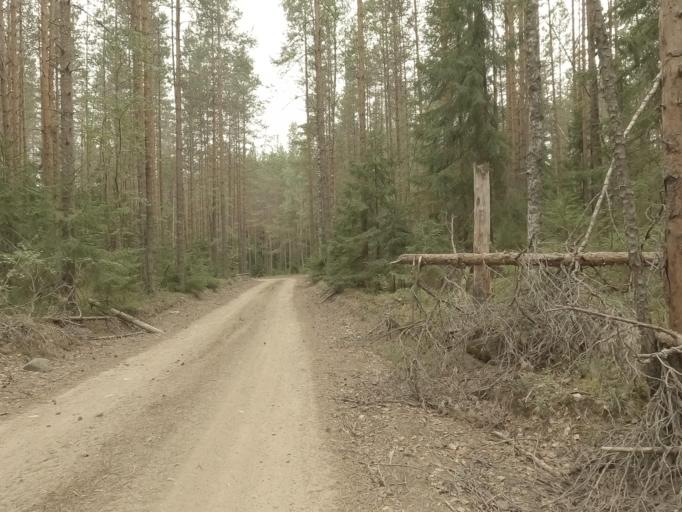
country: RU
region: Leningrad
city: Kamennogorsk
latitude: 61.0396
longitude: 29.1867
